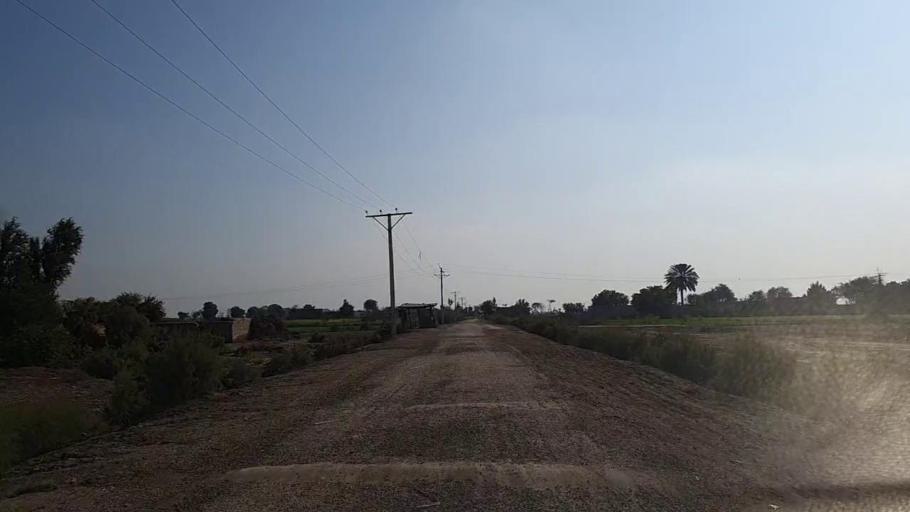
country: PK
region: Sindh
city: Jam Sahib
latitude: 26.2799
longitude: 68.6046
